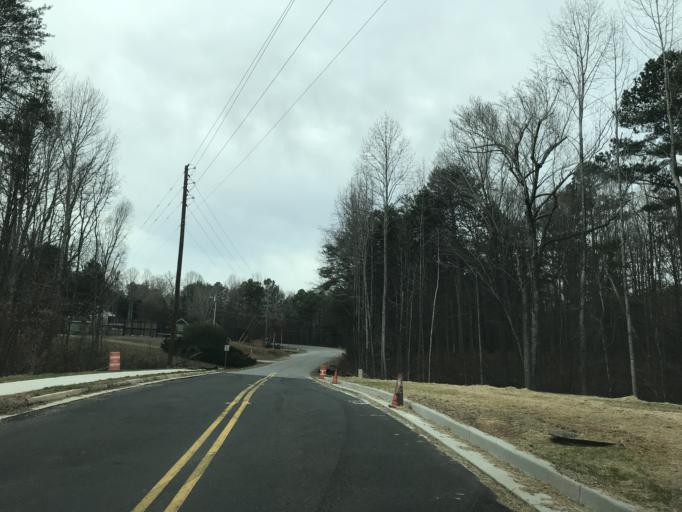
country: US
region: Georgia
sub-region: Forsyth County
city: Cumming
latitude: 34.2285
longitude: -84.0995
